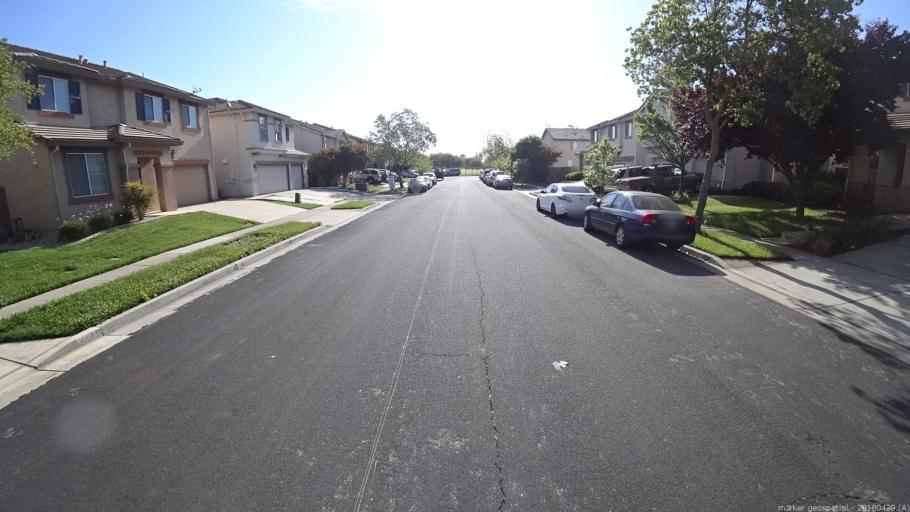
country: US
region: California
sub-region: Yolo County
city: West Sacramento
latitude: 38.5434
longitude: -121.5632
